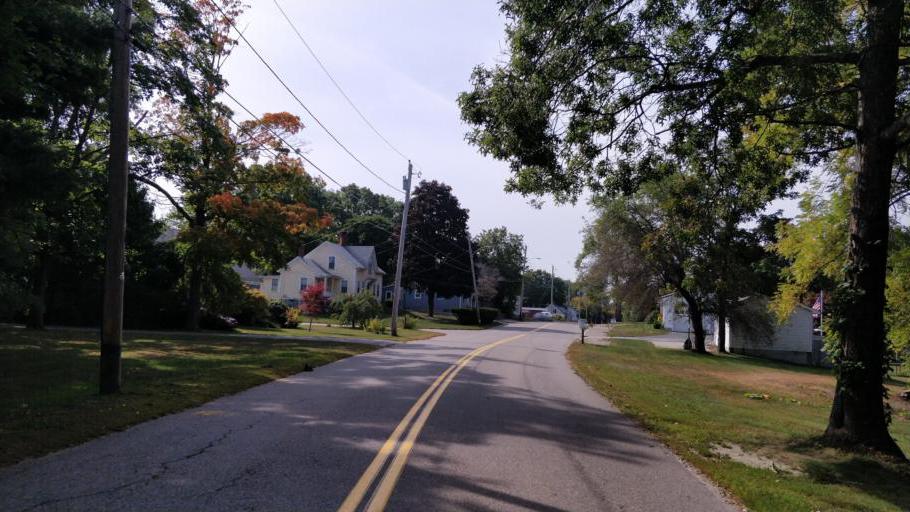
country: US
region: Massachusetts
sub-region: Bristol County
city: North Seekonk
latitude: 41.9071
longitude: -71.3179
